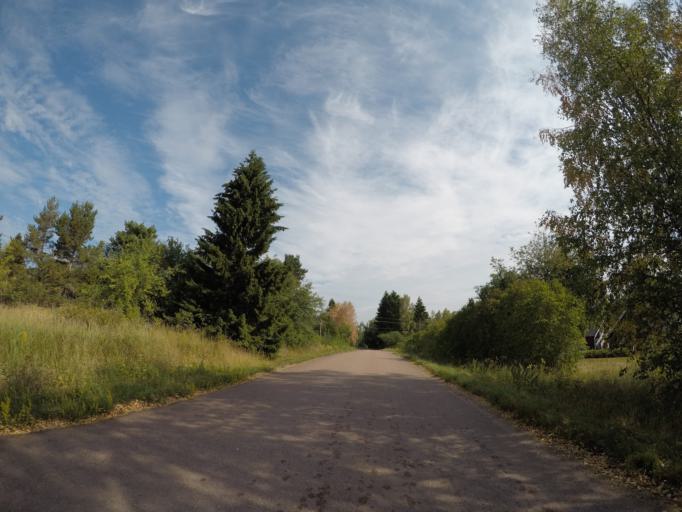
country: AX
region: Alands landsbygd
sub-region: Finstroem
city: Finstroem
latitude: 60.2070
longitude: 19.8743
